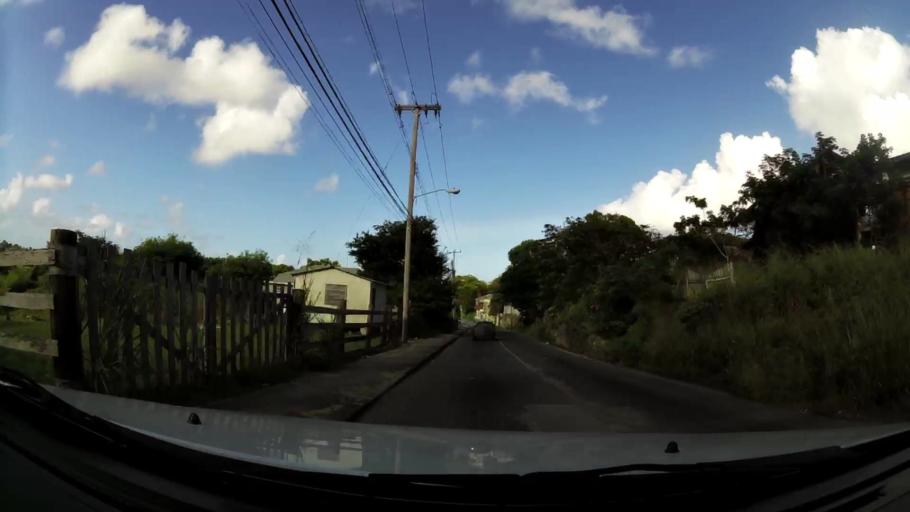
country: BB
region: Saint Michael
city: Bridgetown
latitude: 13.1041
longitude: -59.5868
